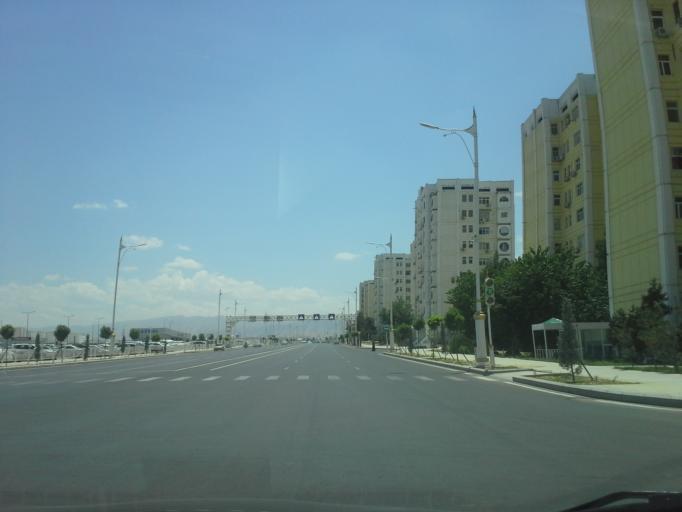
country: TM
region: Ahal
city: Ashgabat
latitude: 37.9061
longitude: 58.3977
